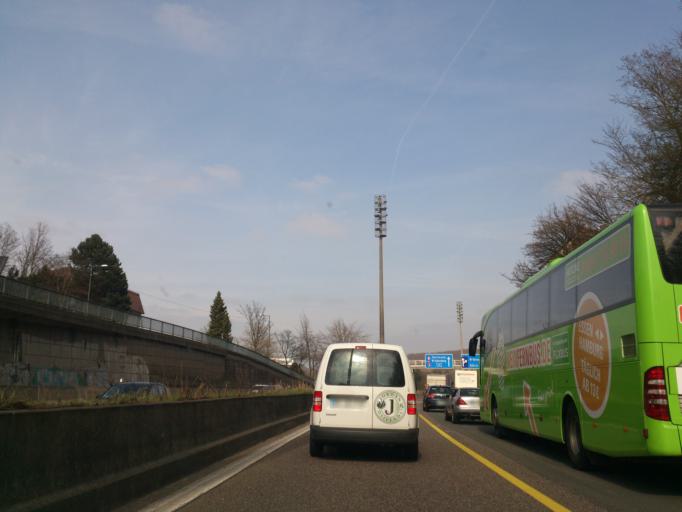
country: DE
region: North Rhine-Westphalia
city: Wulfrath
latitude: 51.2470
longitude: 7.0975
